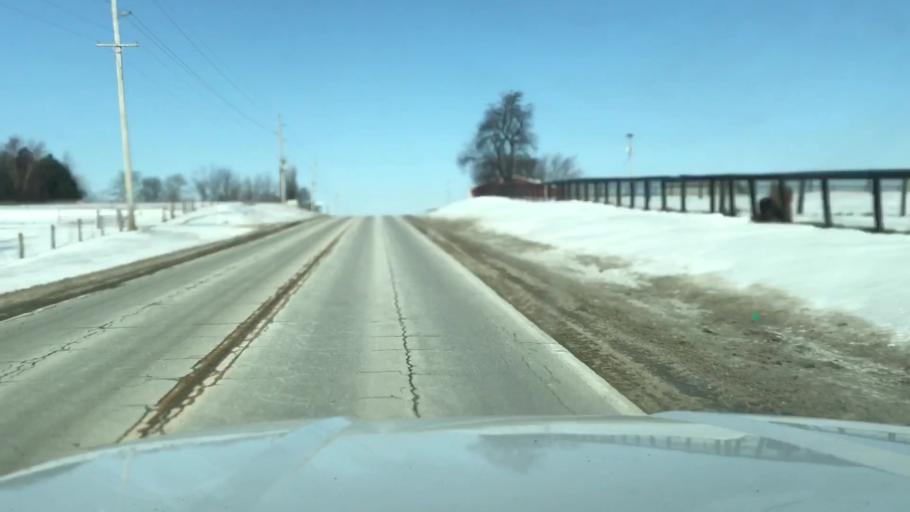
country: US
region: Missouri
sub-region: Andrew County
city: Savannah
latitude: 39.9531
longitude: -94.8477
